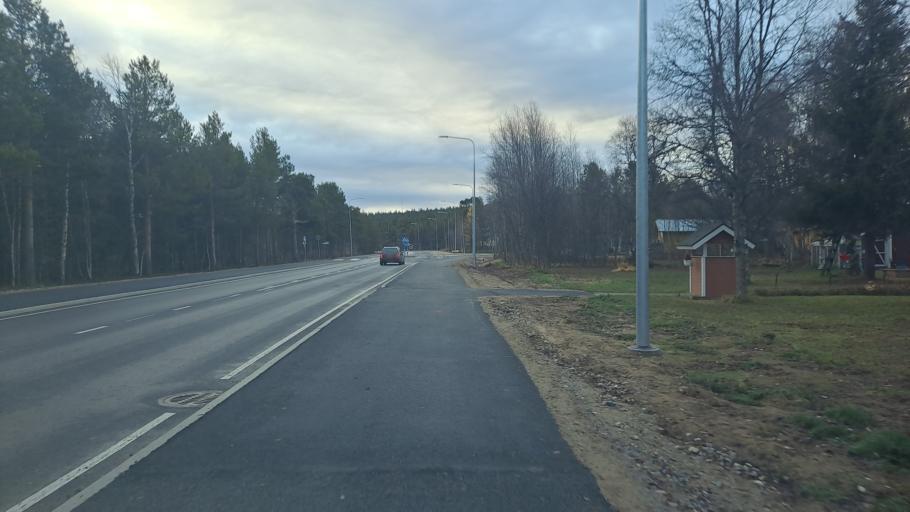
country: FI
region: Lapland
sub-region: Pohjois-Lappi
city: Inari
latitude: 68.9043
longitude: 27.0318
